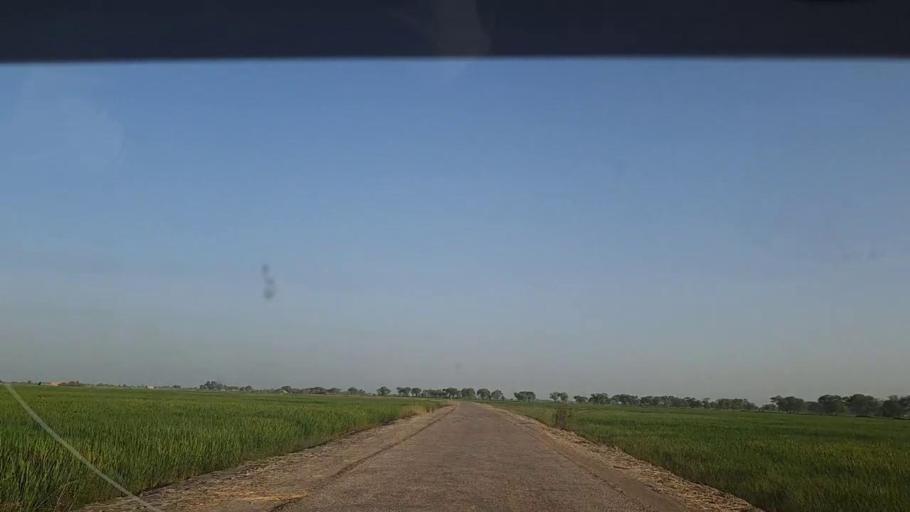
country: PK
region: Sindh
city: Thul
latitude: 28.1880
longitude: 68.8732
